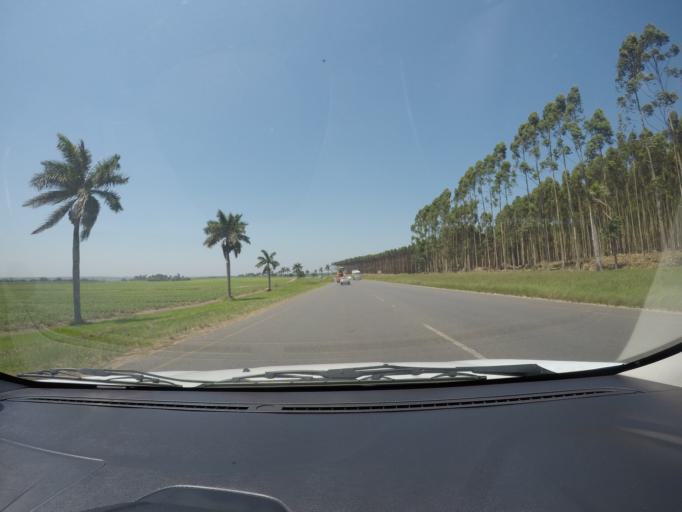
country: ZA
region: KwaZulu-Natal
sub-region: uThungulu District Municipality
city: eSikhawini
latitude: -28.8175
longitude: 31.9527
